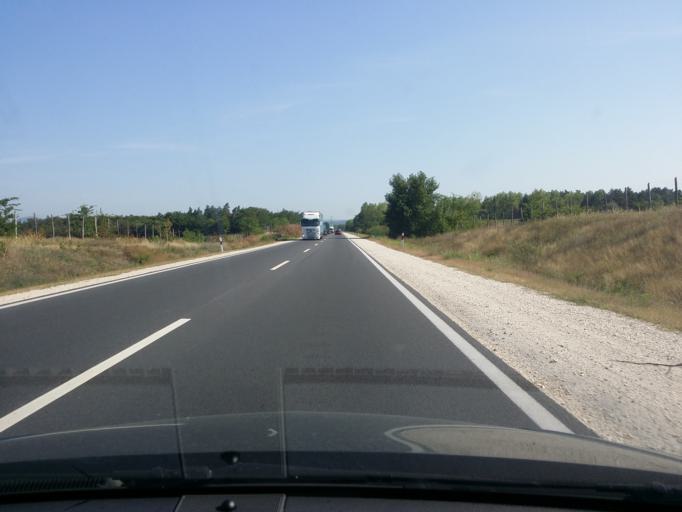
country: HU
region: Pest
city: God
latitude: 47.6693
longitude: 19.1669
